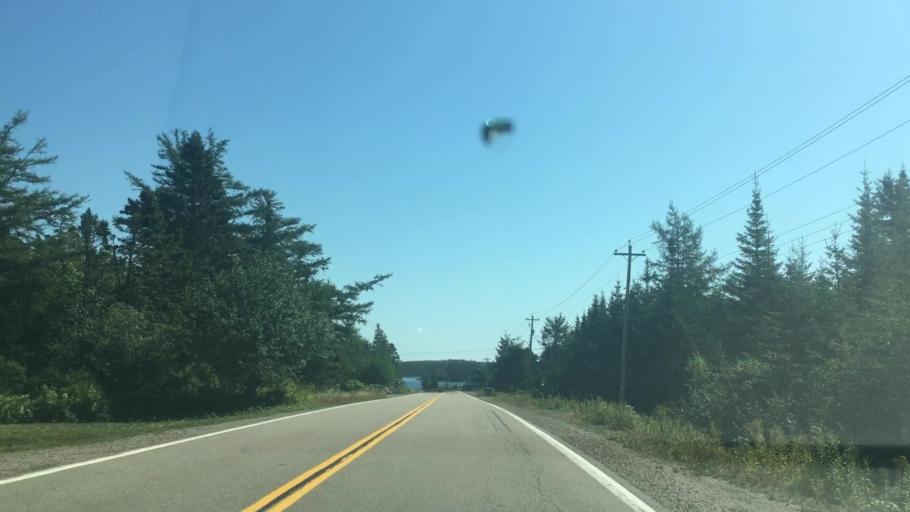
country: CA
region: Nova Scotia
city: Antigonish
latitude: 45.0239
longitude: -62.0224
